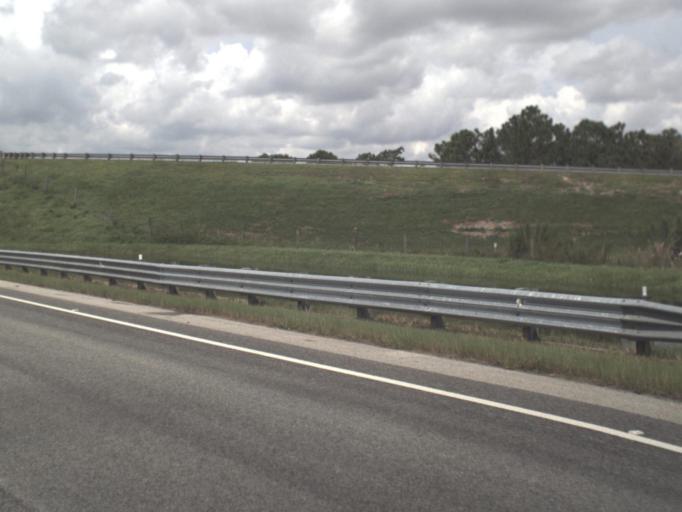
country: US
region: Florida
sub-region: Charlotte County
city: Charlotte Park
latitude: 26.8842
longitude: -81.9902
